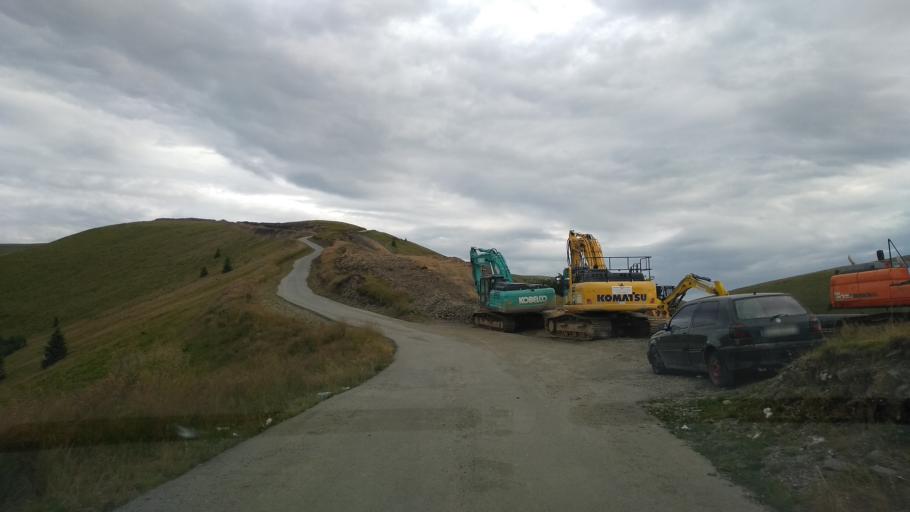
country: RO
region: Hunedoara
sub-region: Municipiul  Vulcan
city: Jiu-Paroseni
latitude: 45.3171
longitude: 23.3037
